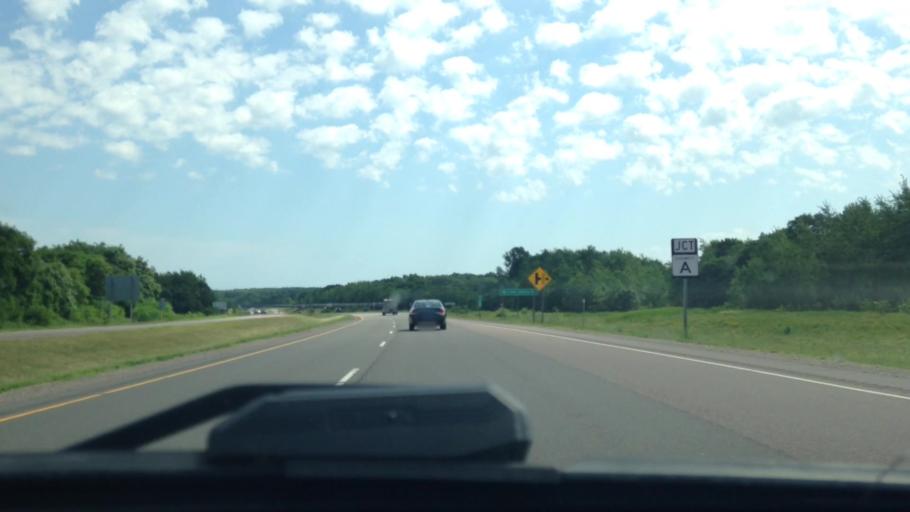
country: US
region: Wisconsin
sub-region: Washburn County
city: Spooner
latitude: 45.8576
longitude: -91.8512
